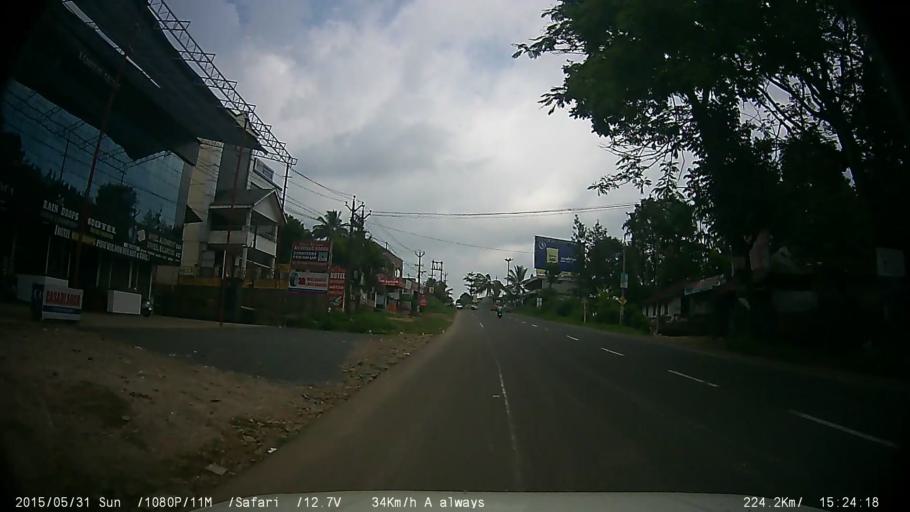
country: IN
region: Kerala
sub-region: Wayanad
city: Panamaram
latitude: 11.6585
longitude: 76.2469
